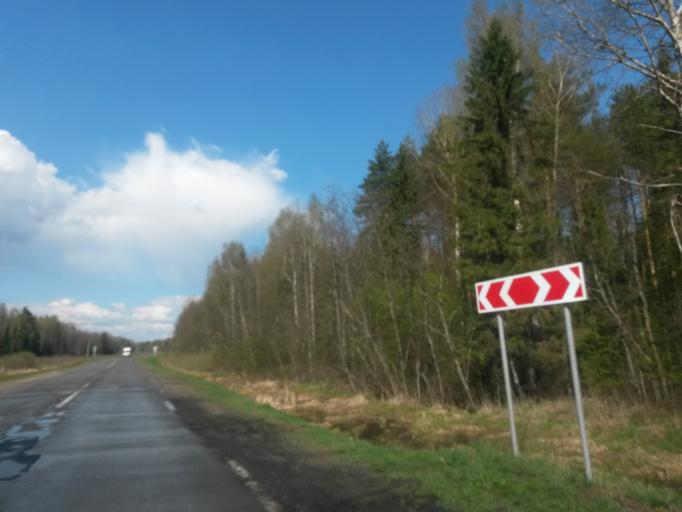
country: RU
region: Jaroslavl
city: Tutayev
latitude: 57.9494
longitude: 39.4982
